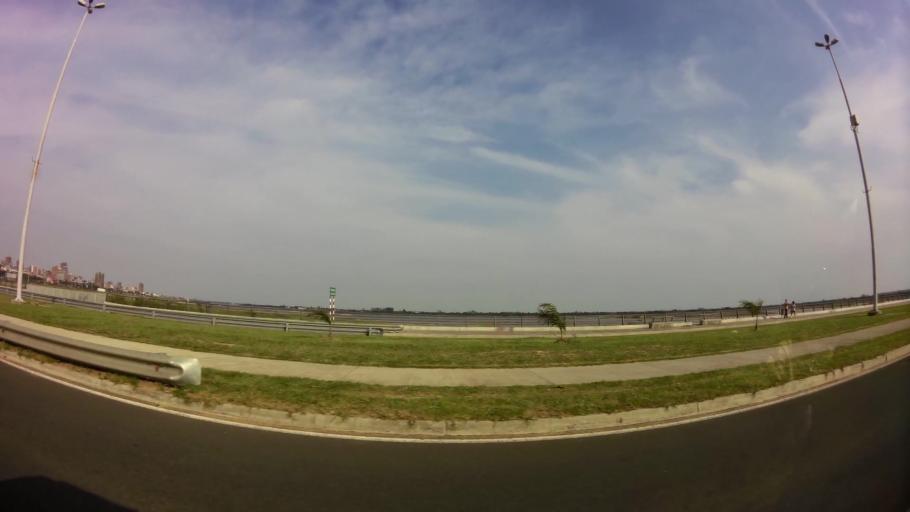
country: PY
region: Asuncion
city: Asuncion
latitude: -25.2756
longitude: -57.6177
